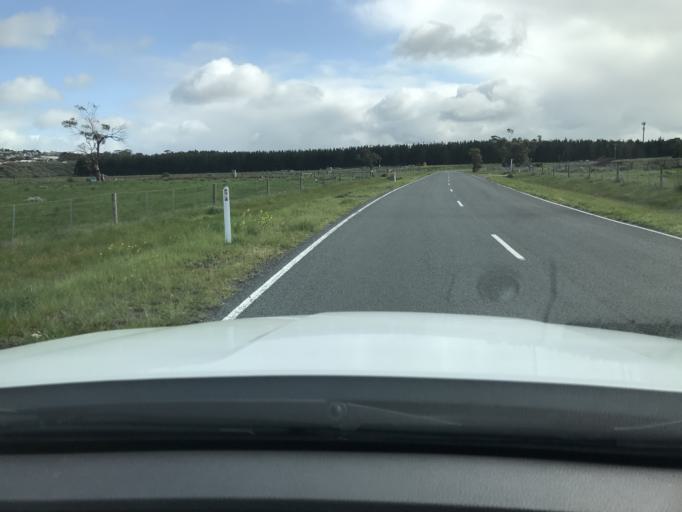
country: AU
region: Victoria
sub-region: Hume
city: Craigieburn
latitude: -37.5790
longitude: 144.9443
